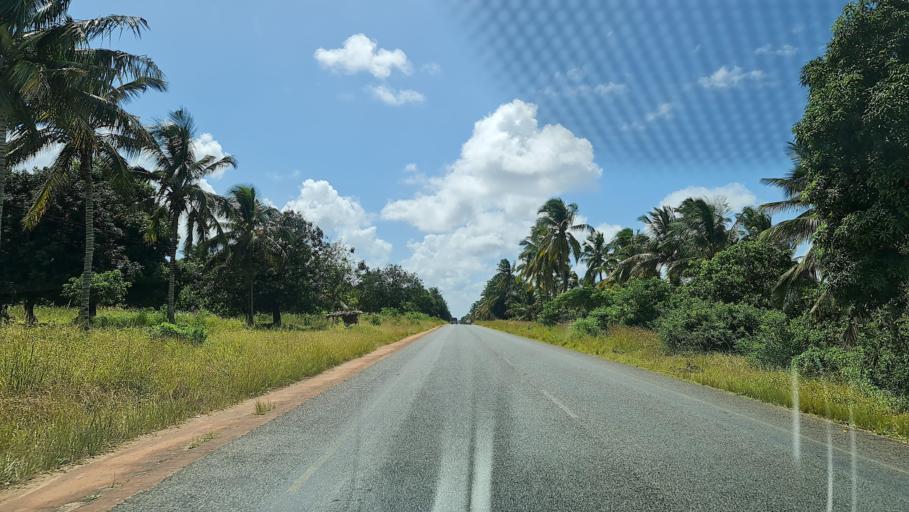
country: MZ
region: Inhambane
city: Maxixe
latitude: -24.5425
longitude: 34.8976
